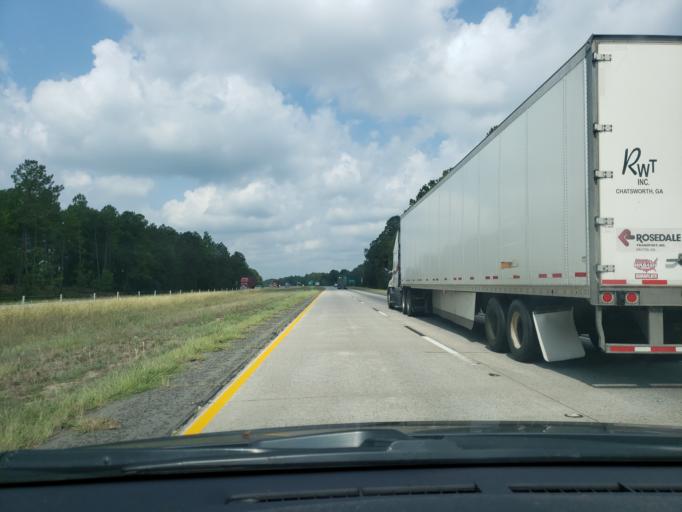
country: US
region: Georgia
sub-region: Treutlen County
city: Soperton
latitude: 32.4335
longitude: -82.5945
